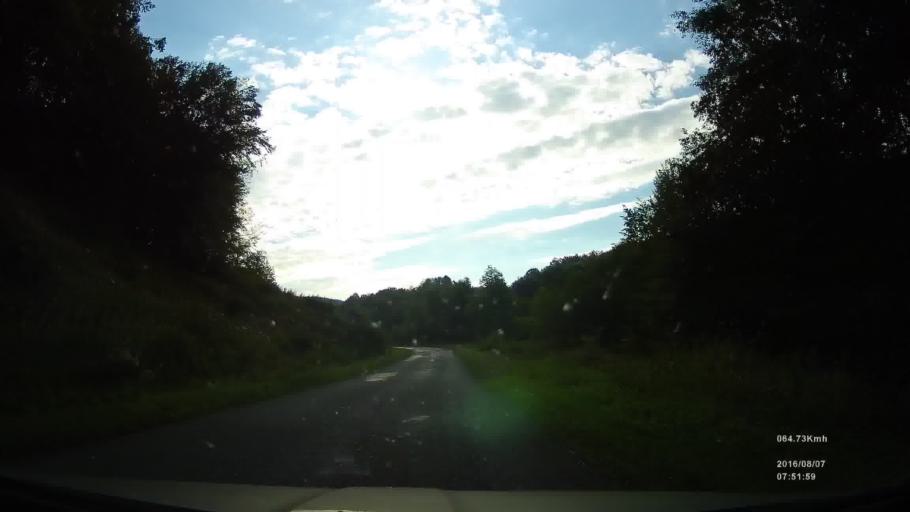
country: SK
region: Presovsky
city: Medzilaborce
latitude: 49.3071
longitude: 21.7927
